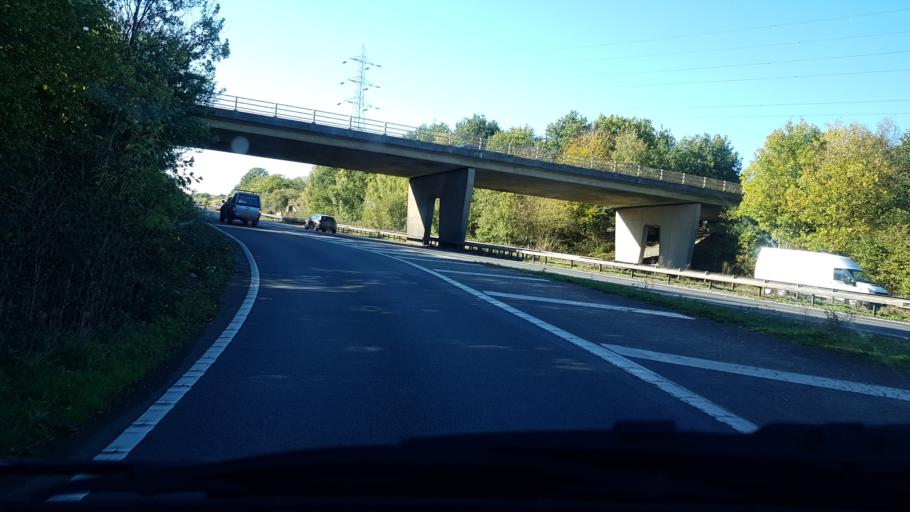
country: GB
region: England
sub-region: Surrey
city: Send
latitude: 51.2794
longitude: -0.5088
